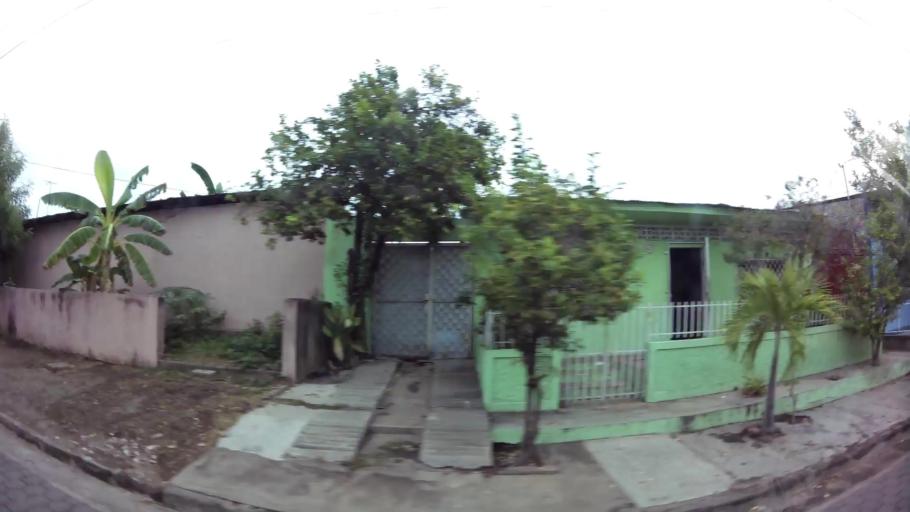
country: NI
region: Granada
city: Granada
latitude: 11.9343
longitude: -85.9620
